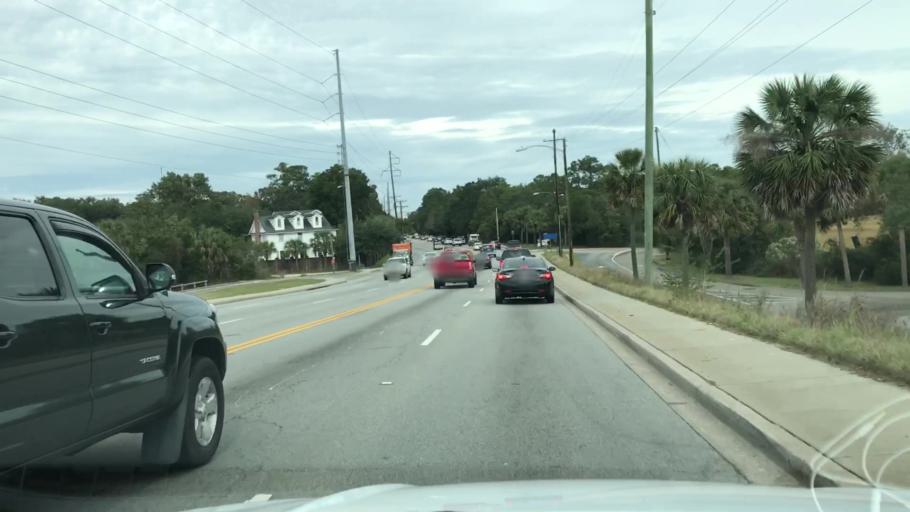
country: US
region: South Carolina
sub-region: Charleston County
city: Charleston
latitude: 32.7684
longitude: -79.9737
